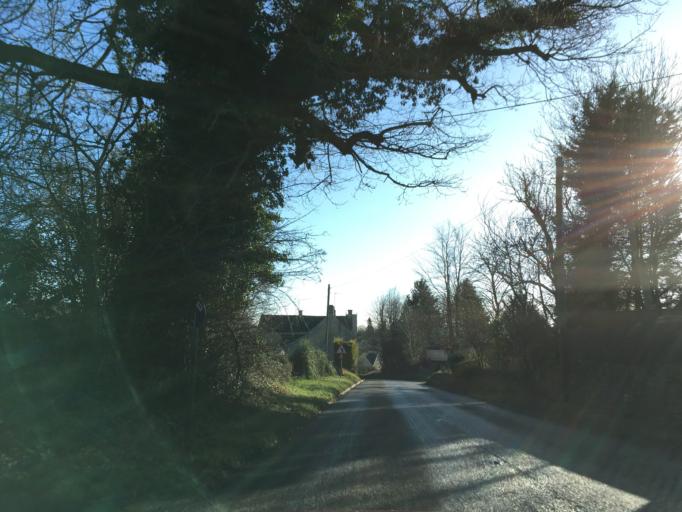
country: GB
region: England
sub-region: Wiltshire
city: Nettleton
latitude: 51.5158
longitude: -2.2718
